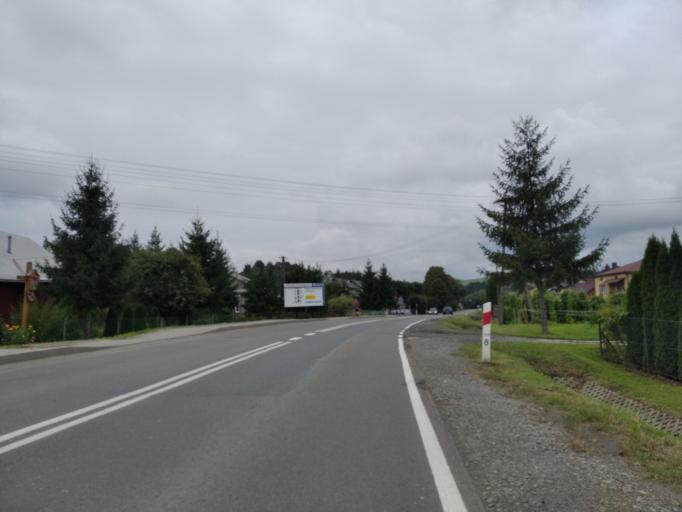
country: PL
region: Subcarpathian Voivodeship
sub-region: Powiat przemyski
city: Bircza
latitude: 49.6910
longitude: 22.4664
